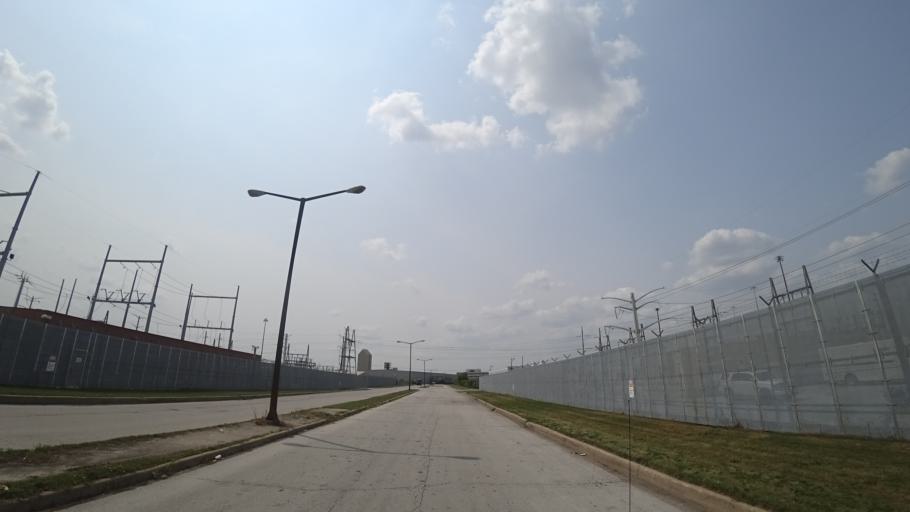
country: US
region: Illinois
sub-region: Cook County
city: Cicero
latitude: 41.8282
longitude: -87.7261
